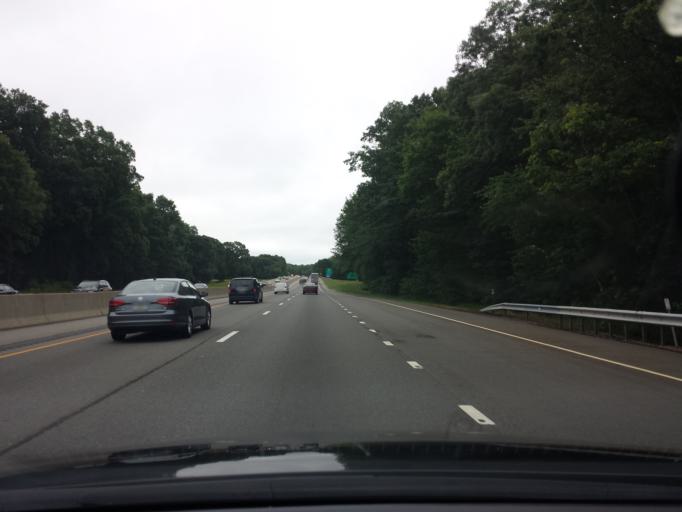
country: US
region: Connecticut
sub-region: New Haven County
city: Madison Center
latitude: 41.2882
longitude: -72.6199
